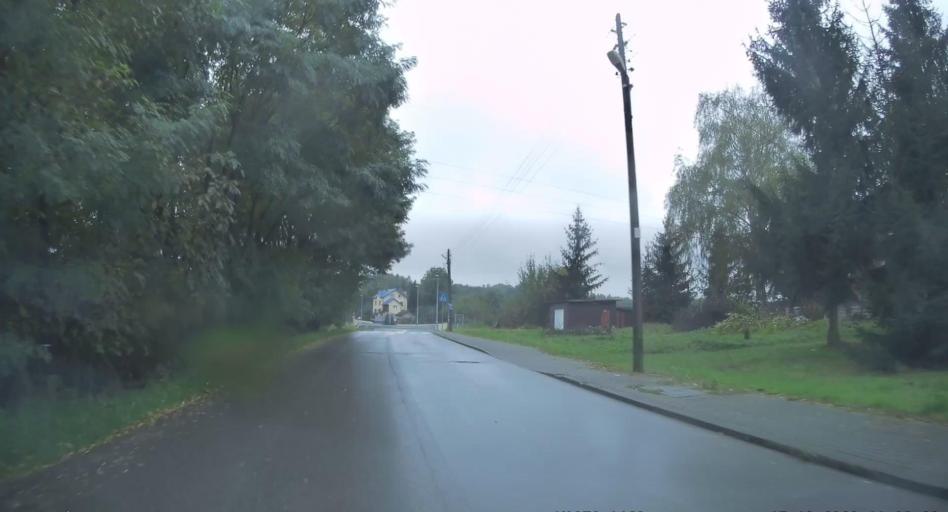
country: PL
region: Lesser Poland Voivodeship
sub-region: Powiat krakowski
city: Ochojno
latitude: 50.0017
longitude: 19.9928
